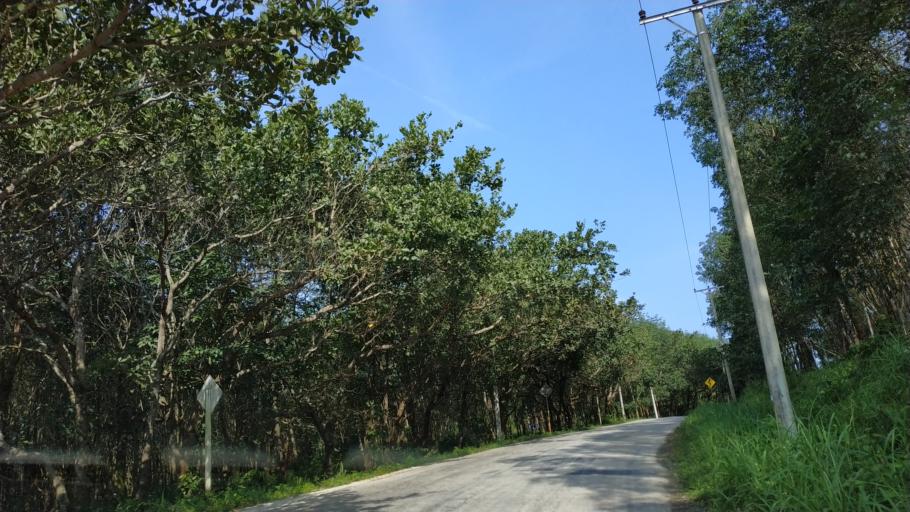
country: MM
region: Tanintharyi
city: Dawei
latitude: 14.5908
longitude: 98.0690
